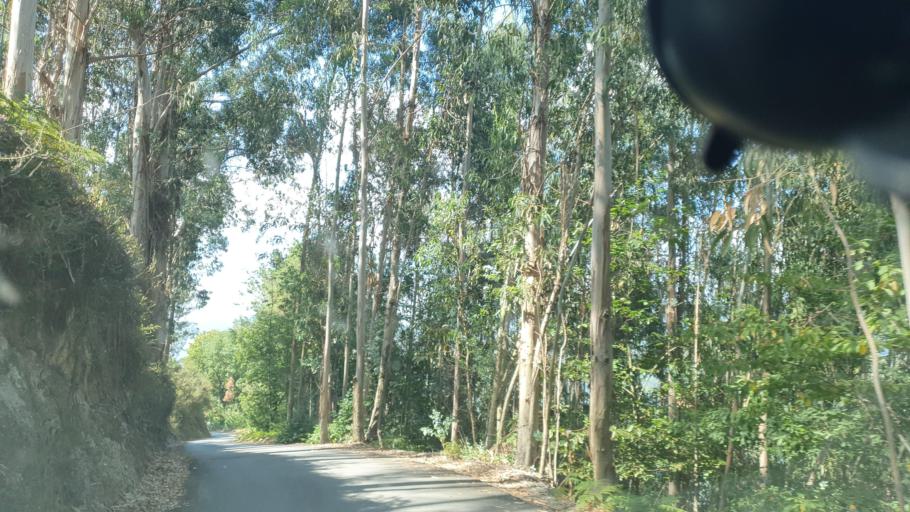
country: PT
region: Braga
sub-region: Vieira do Minho
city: Vieira do Minho
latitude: 41.6738
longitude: -8.1341
